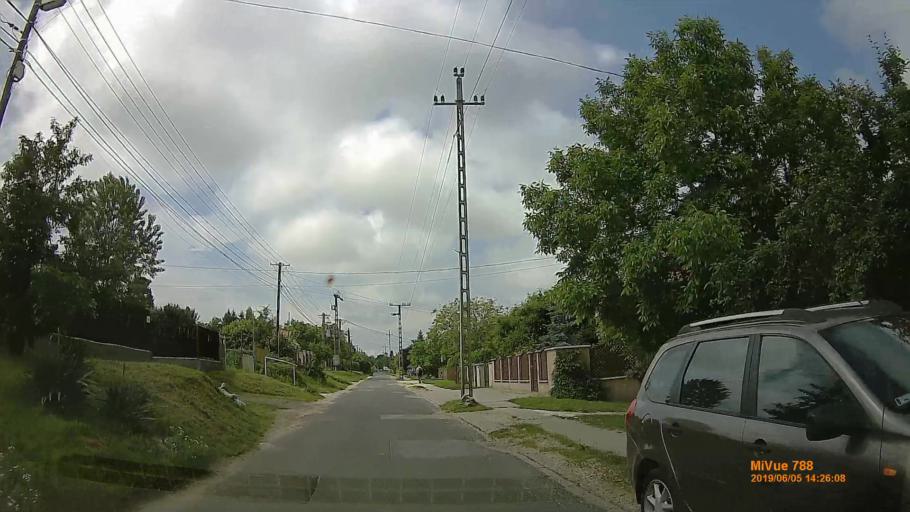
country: HU
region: Pest
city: Kistarcsa
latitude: 47.5572
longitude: 19.2670
